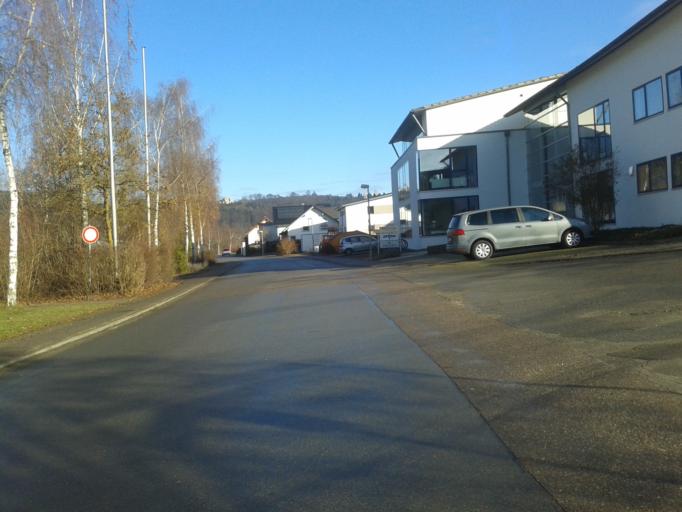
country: DE
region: Baden-Wuerttemberg
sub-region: Tuebingen Region
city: Erbach
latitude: 48.4132
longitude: 9.8726
